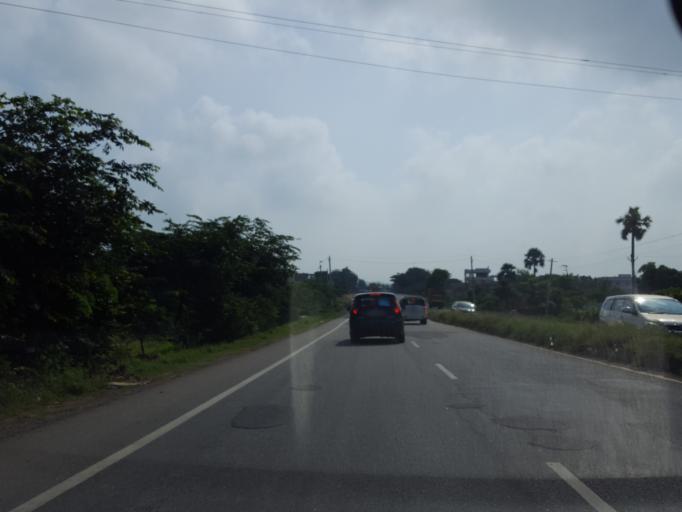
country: IN
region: Telangana
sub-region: Rangareddi
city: Ghatkesar
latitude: 17.2921
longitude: 78.7571
